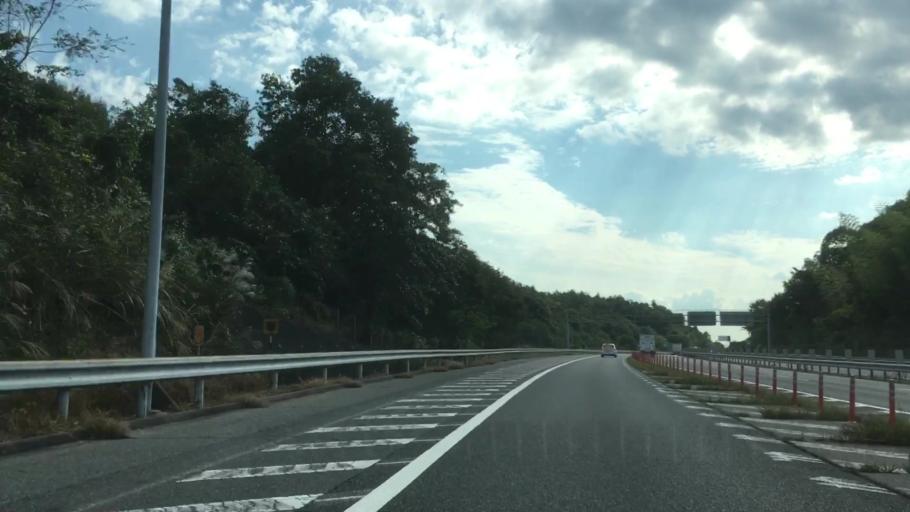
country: JP
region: Hiroshima
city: Miyajima
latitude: 34.3294
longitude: 132.2937
